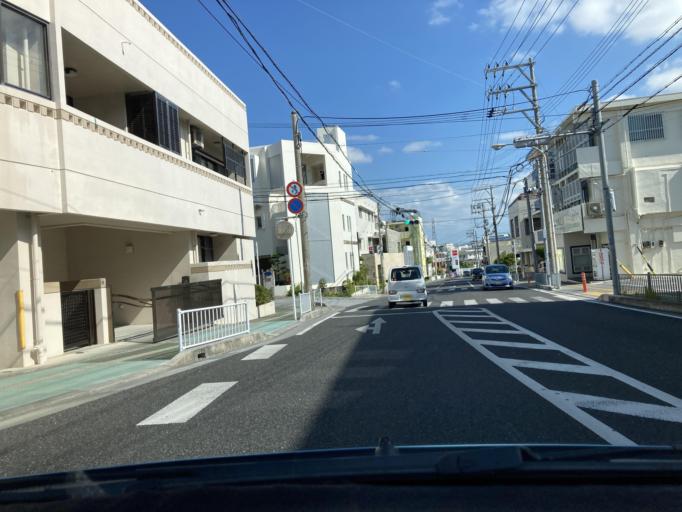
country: JP
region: Okinawa
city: Tomigusuku
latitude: 26.1900
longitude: 127.6692
